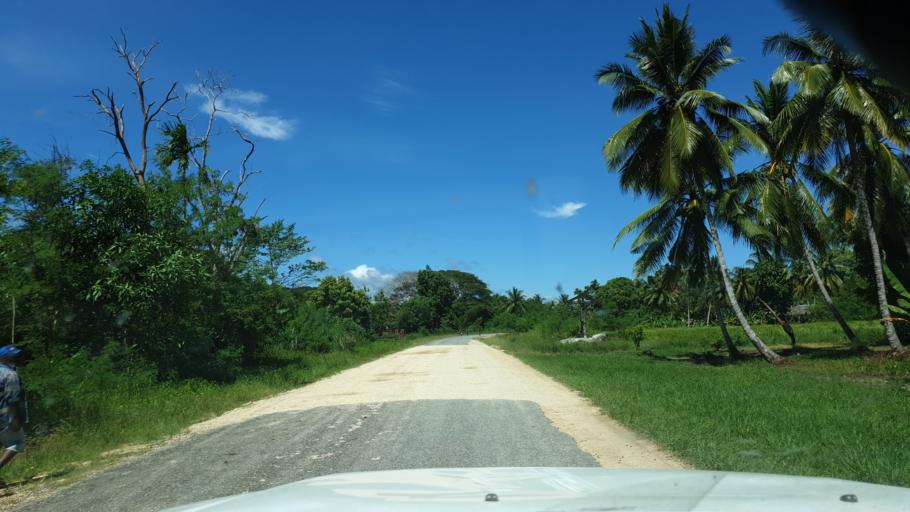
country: PG
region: Madang
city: Madang
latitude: -4.4492
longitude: 145.3632
